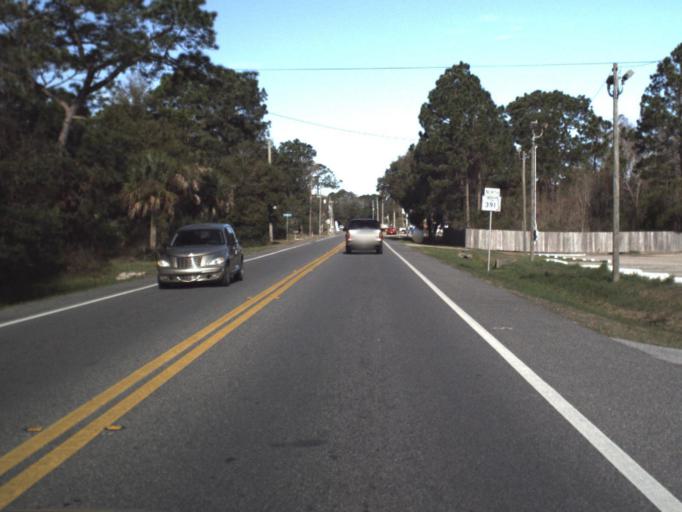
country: US
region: Florida
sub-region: Bay County
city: Panama City
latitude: 30.1828
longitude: -85.6681
